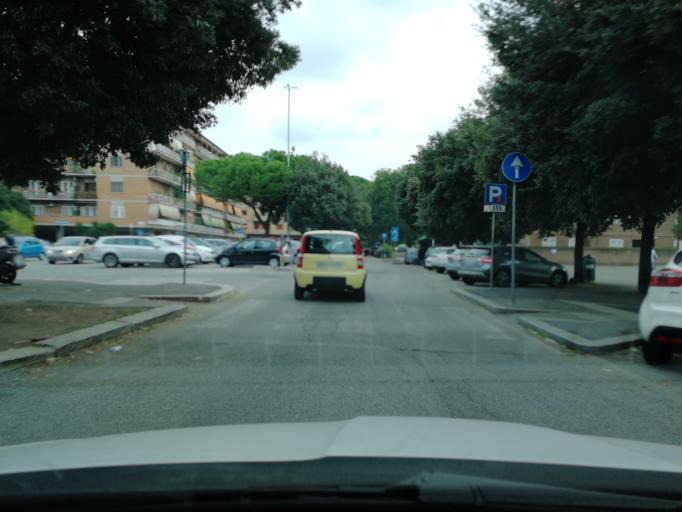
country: IT
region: Latium
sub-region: Citta metropolitana di Roma Capitale
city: Rome
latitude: 41.8530
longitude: 12.5583
